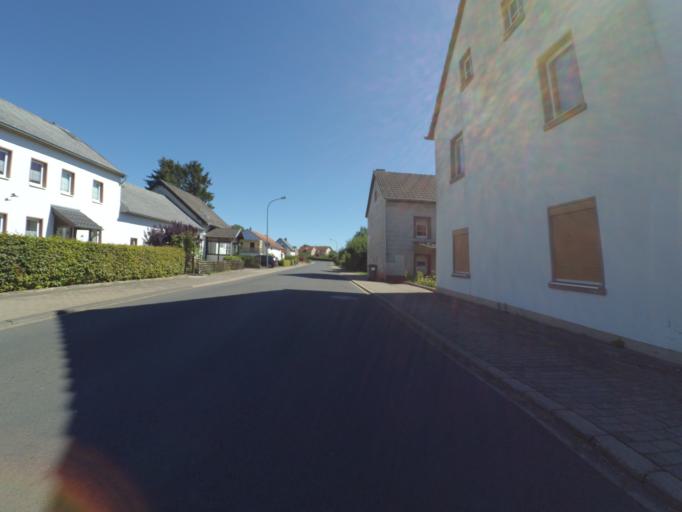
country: DE
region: Rheinland-Pfalz
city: Feusdorf
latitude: 50.3491
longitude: 6.6146
